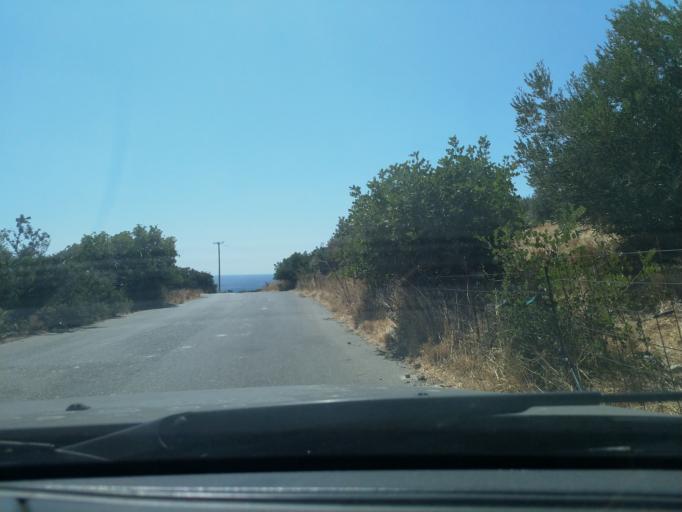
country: GR
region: Crete
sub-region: Nomos Rethymnis
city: Agia Galini
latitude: 35.1222
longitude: 24.5546
